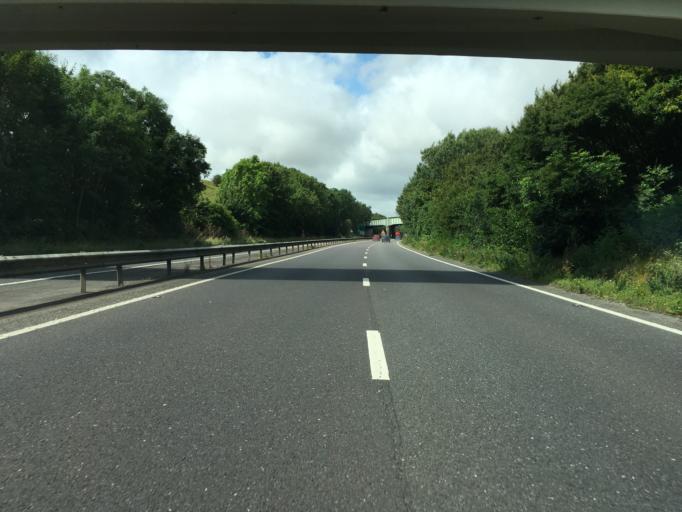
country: GB
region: England
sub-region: East Sussex
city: Lewes
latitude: 50.8669
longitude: -0.0134
